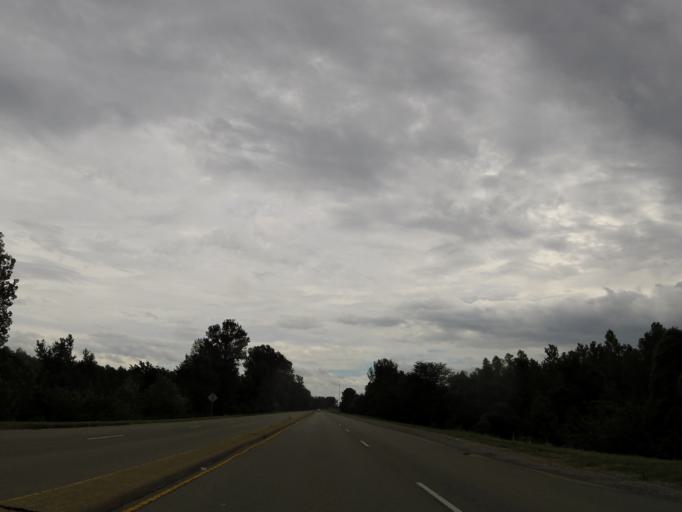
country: US
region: Illinois
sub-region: Alexander County
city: Cairo
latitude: 36.9938
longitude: -89.1596
